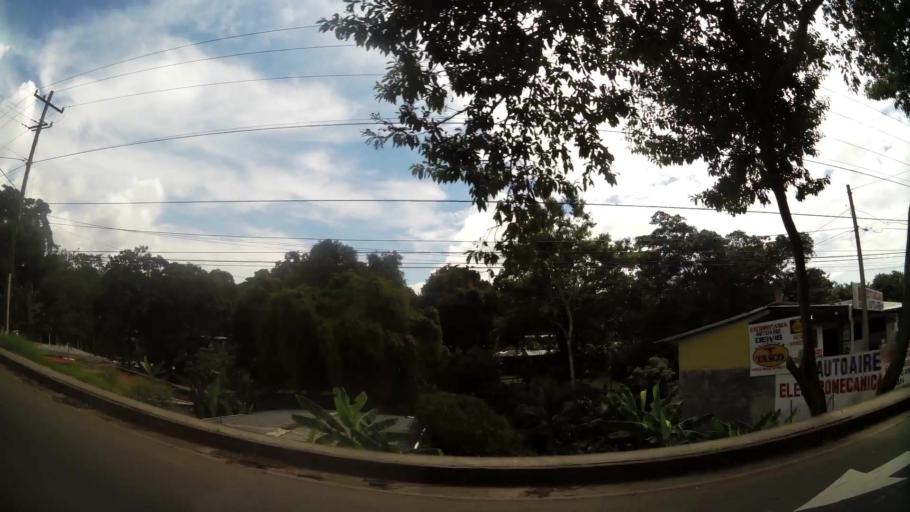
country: PA
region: Panama
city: Vista Alegre
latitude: 8.9368
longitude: -79.6848
